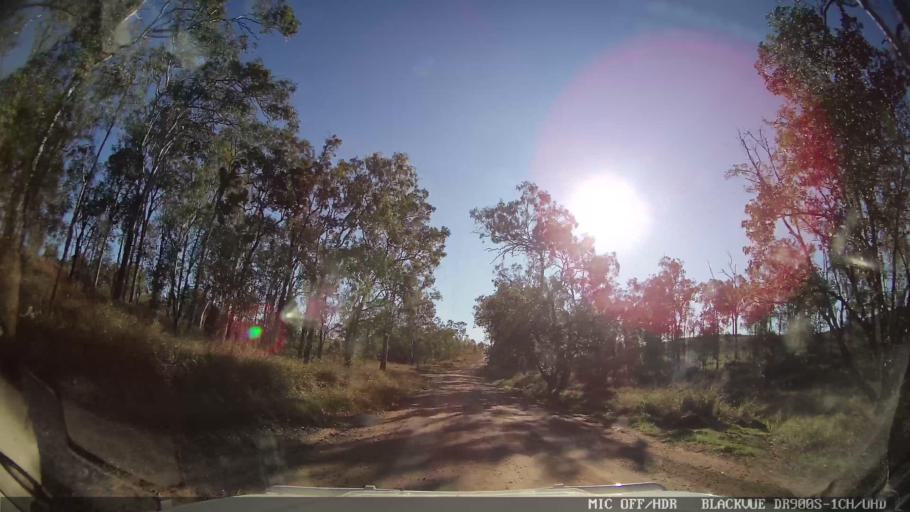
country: AU
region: Queensland
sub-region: Bundaberg
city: Sharon
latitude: -24.8030
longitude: 151.6474
